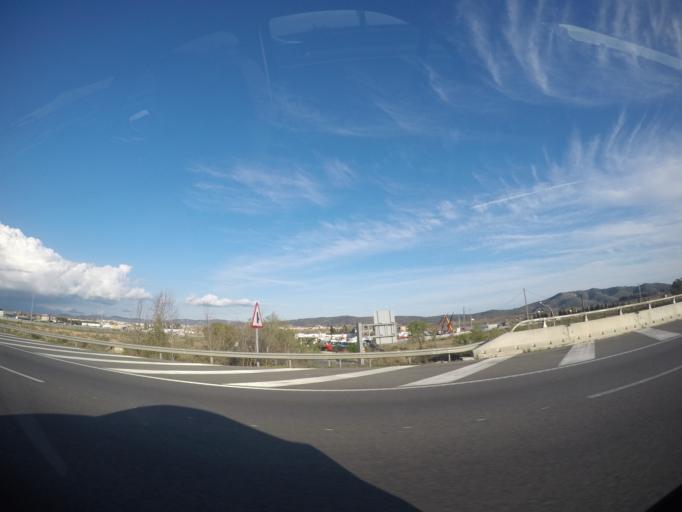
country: ES
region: Catalonia
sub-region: Provincia de Barcelona
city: Vilafranca del Penedes
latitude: 41.3476
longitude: 1.7179
